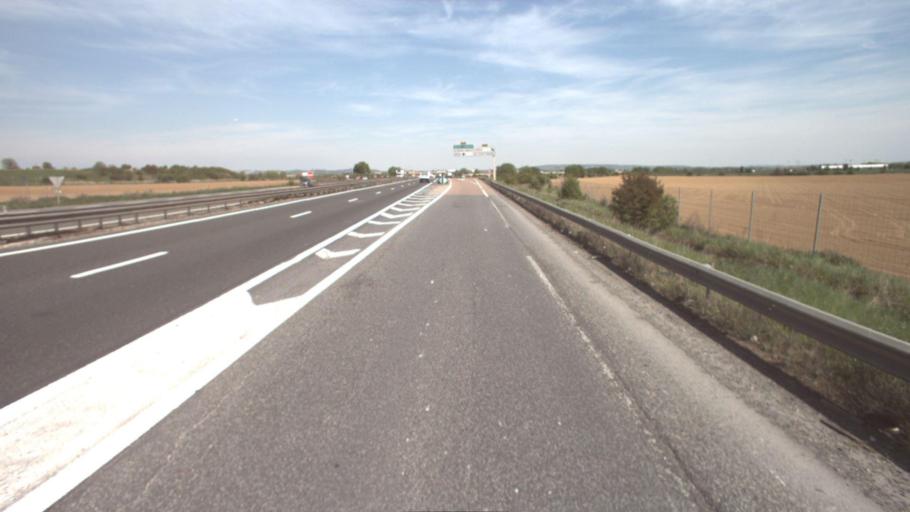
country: FR
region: Ile-de-France
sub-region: Departement de Seine-et-Marne
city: Mitry-Mory
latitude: 48.9958
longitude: 2.6258
